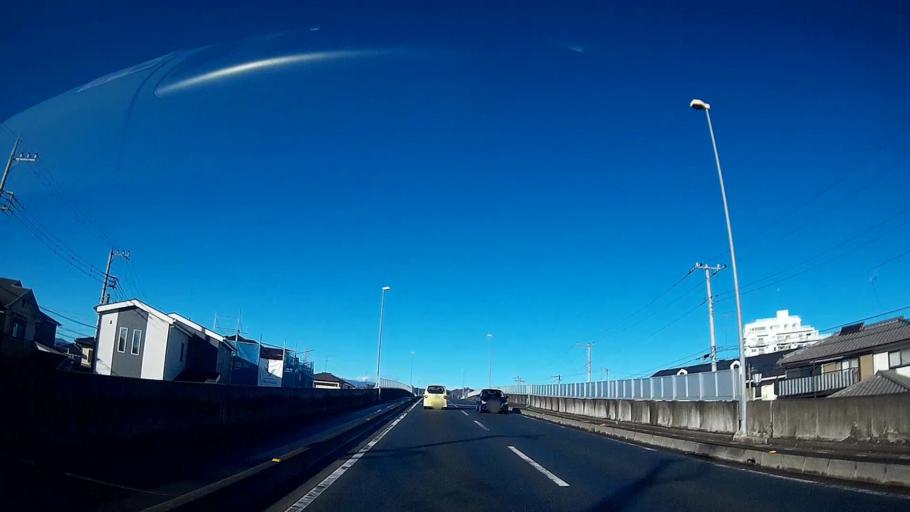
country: JP
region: Saitama
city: Hanno
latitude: 35.8599
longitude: 139.3284
